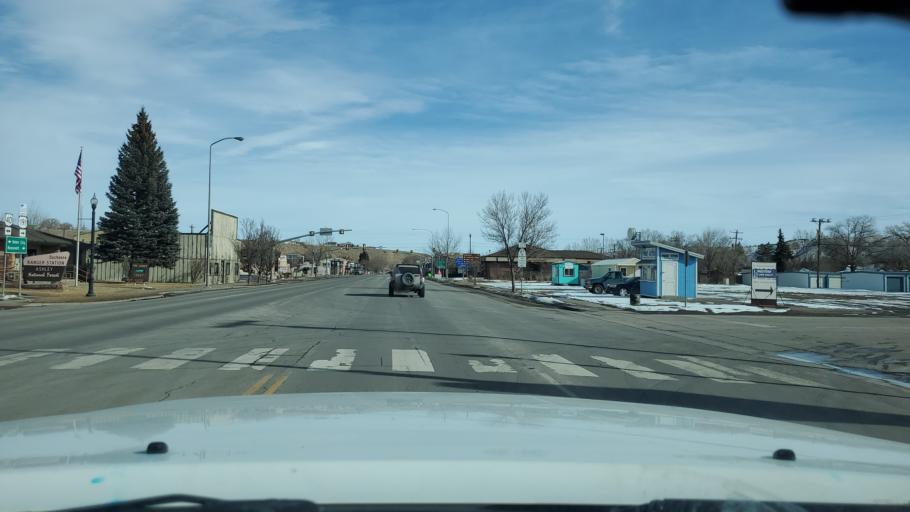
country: US
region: Utah
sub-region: Duchesne County
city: Duchesne
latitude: 40.1634
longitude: -110.4033
